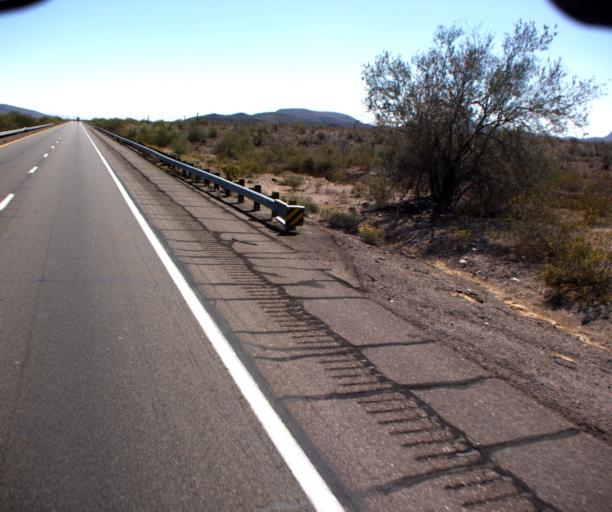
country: US
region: Arizona
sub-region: La Paz County
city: Quartzsite
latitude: 33.6581
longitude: -113.9827
